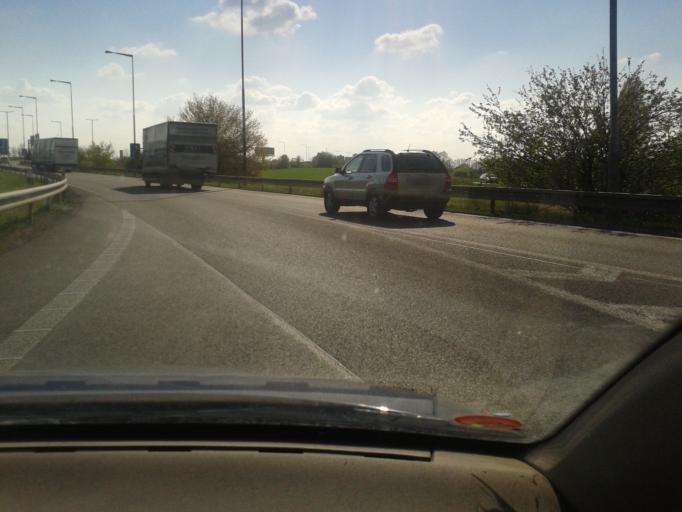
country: CZ
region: Central Bohemia
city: Hostivice
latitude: 50.0505
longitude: 14.2729
